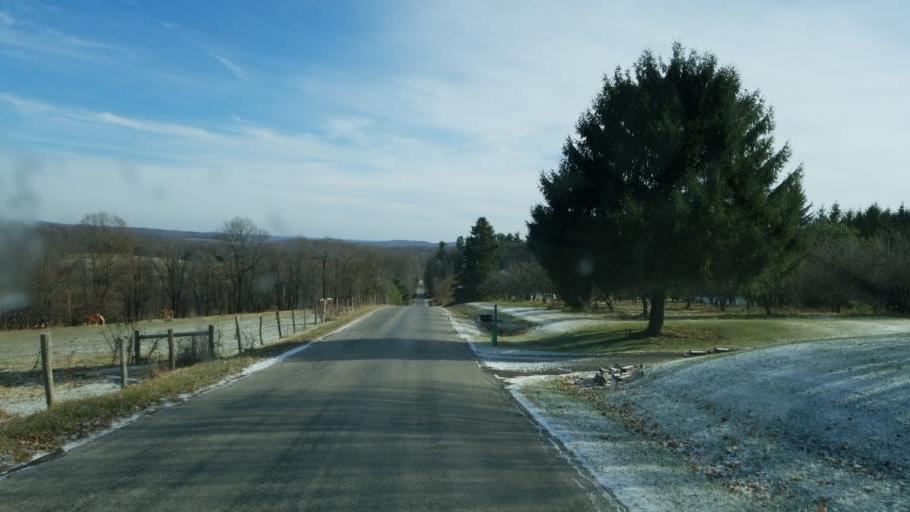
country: US
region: Ohio
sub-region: Sandusky County
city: Bellville
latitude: 40.5868
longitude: -82.5626
